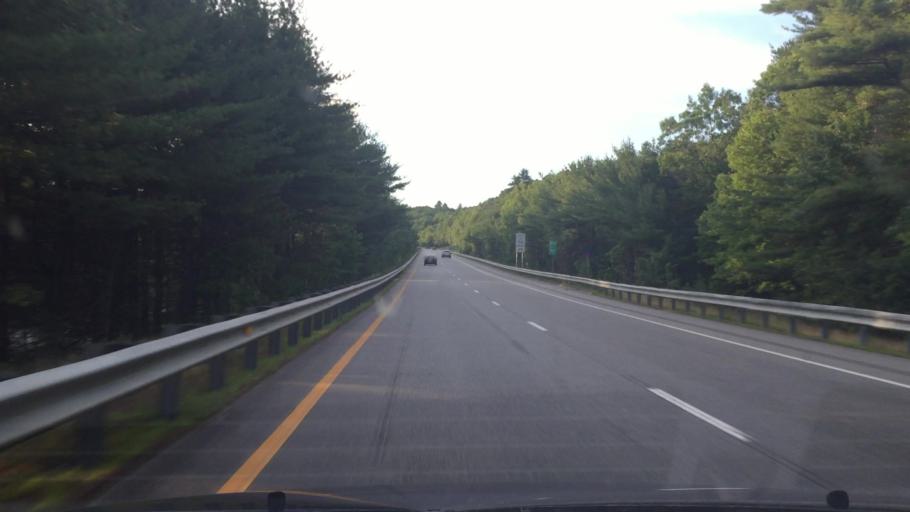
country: US
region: New Hampshire
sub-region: Grafton County
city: Ashland
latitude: 43.7067
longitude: -71.6501
